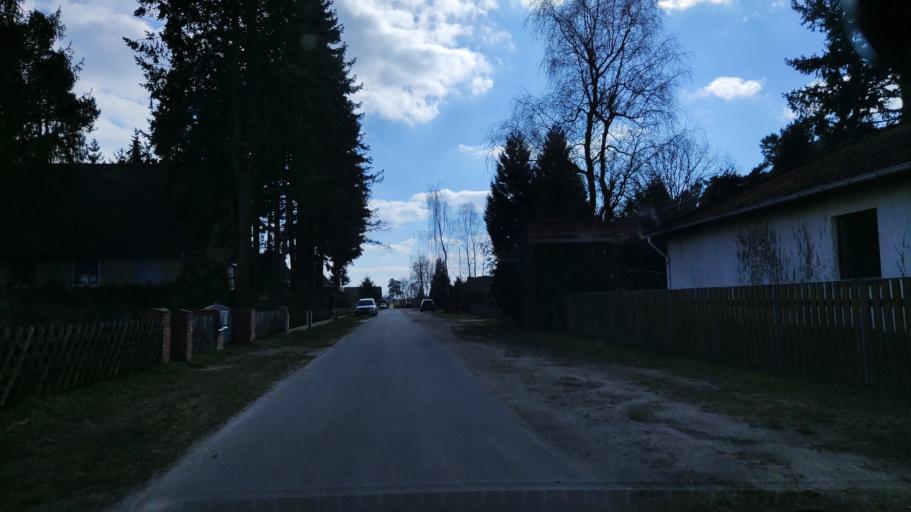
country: DE
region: Lower Saxony
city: Jelmstorf
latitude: 53.1044
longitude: 10.5165
